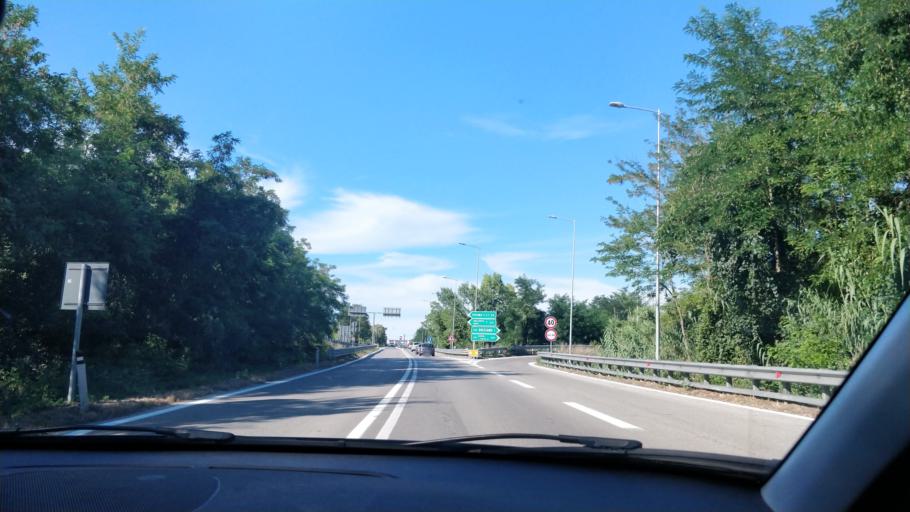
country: IT
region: Abruzzo
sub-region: Provincia di Chieti
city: Casalincontrada
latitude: 42.3375
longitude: 14.1284
